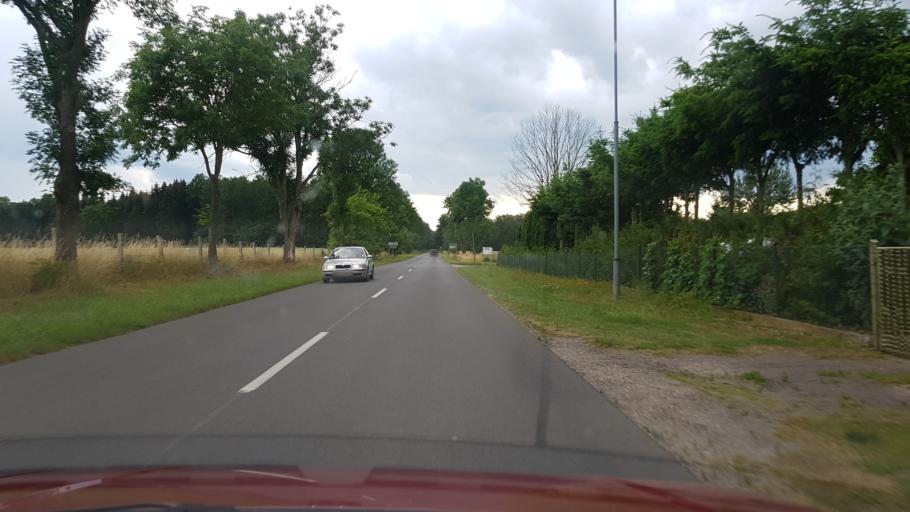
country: PL
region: West Pomeranian Voivodeship
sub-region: Powiat gryficki
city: Gryfice
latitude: 53.8893
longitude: 15.1665
